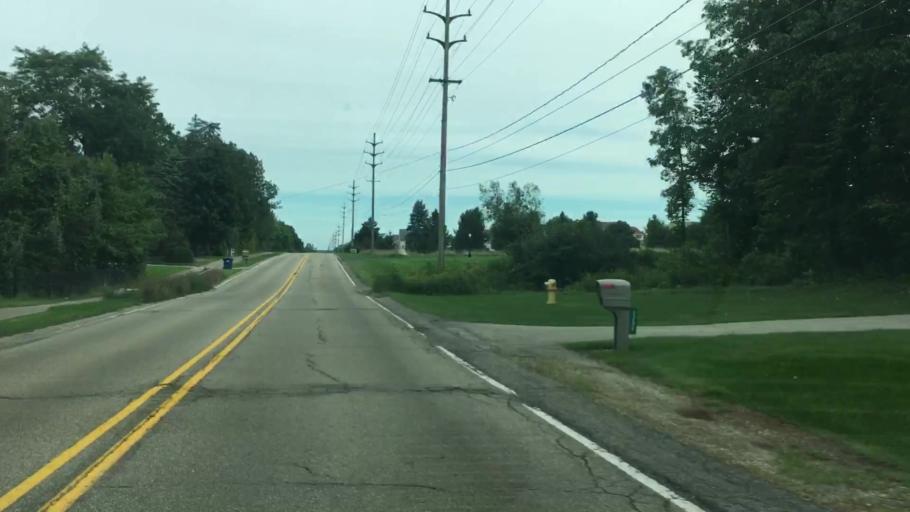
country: US
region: Michigan
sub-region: Ottawa County
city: Jenison
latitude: 42.8708
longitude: -85.7822
